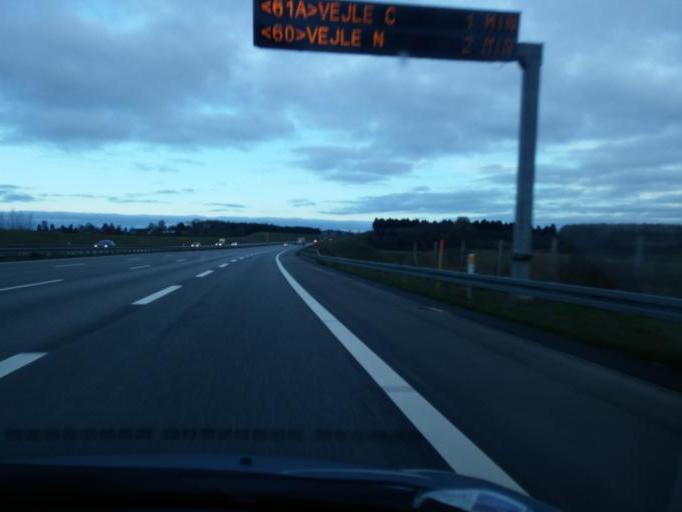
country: DK
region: South Denmark
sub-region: Vejle Kommune
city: Vejle
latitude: 55.6713
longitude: 9.5537
